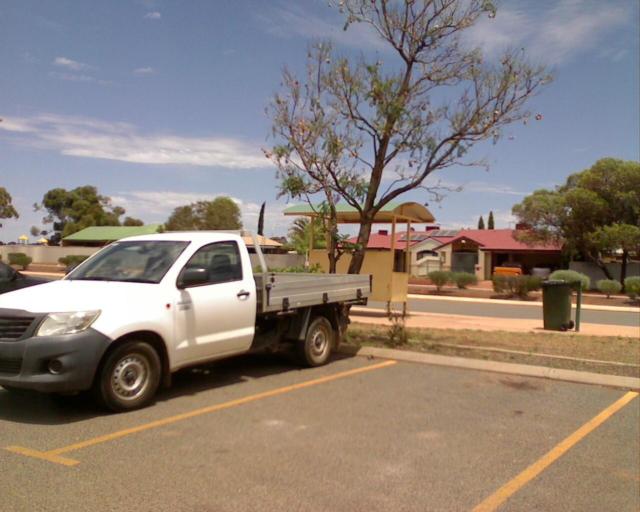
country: AU
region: Western Australia
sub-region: Kalgoorlie/Boulder
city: Boulder
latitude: -30.7752
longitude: 121.4606
